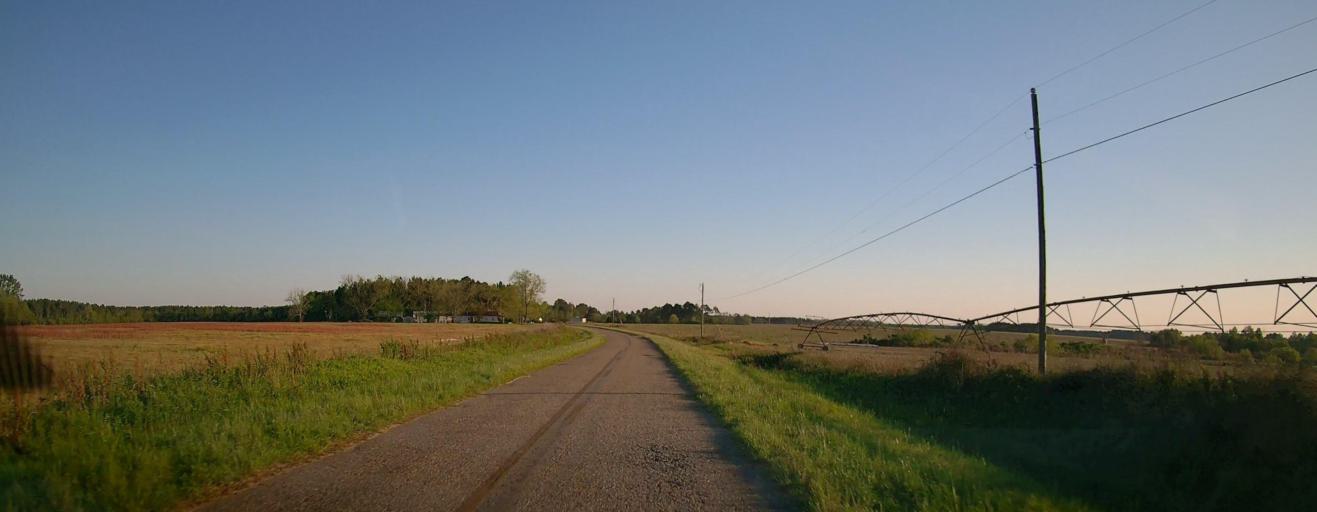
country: US
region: Georgia
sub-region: Ben Hill County
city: Fitzgerald
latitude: 31.6598
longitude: -83.2108
